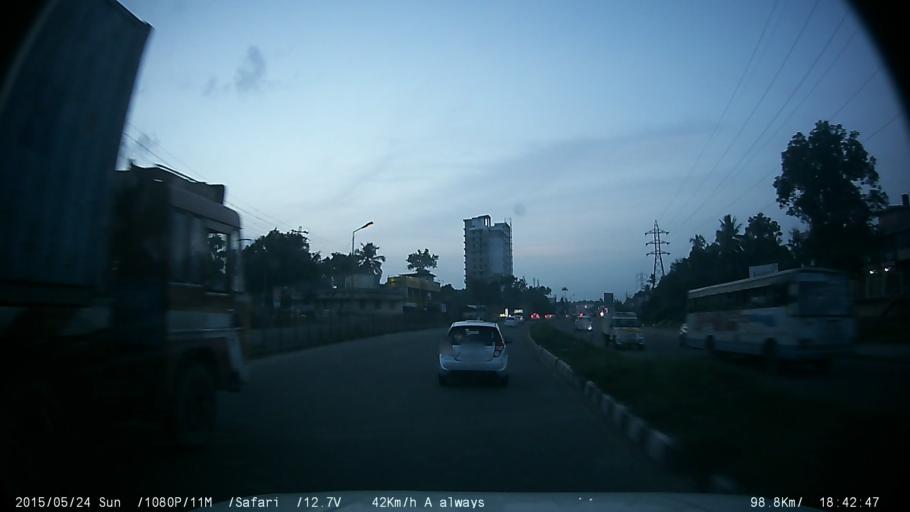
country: IN
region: Kerala
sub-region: Ernakulam
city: Aluva
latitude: 10.1140
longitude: 76.3460
